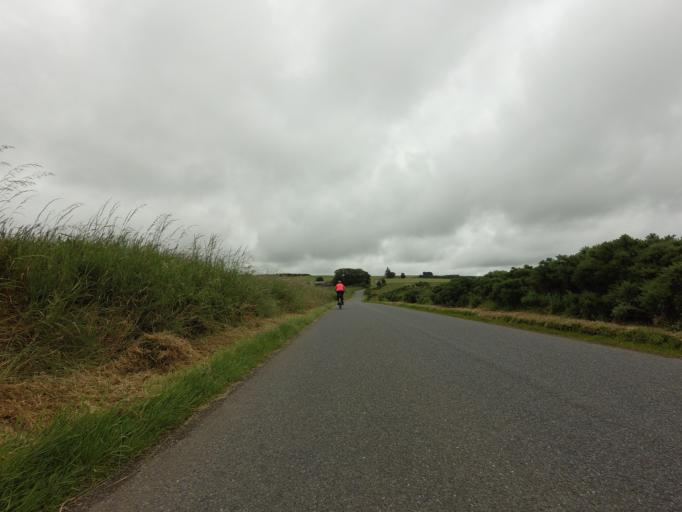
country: GB
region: Scotland
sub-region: Aberdeenshire
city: Turriff
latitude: 57.5427
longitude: -2.2661
